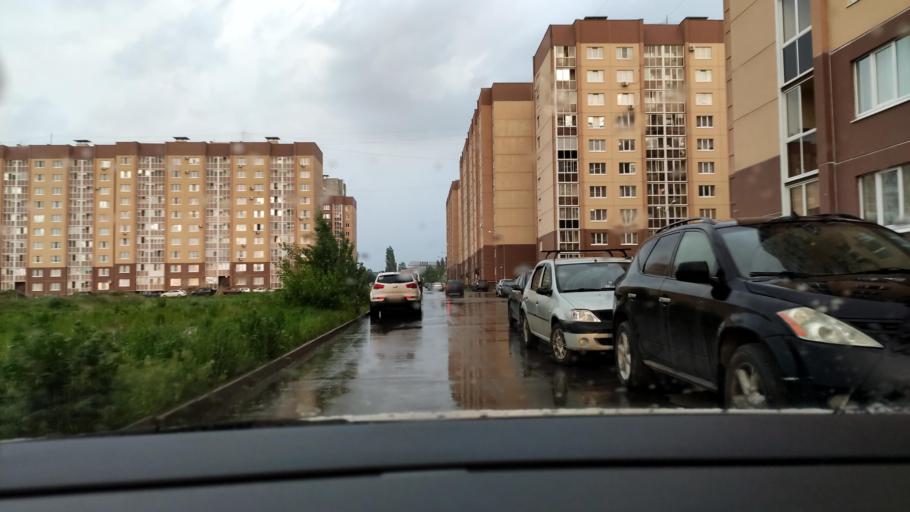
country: RU
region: Voronezj
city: Shilovo
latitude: 51.5723
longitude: 39.1255
